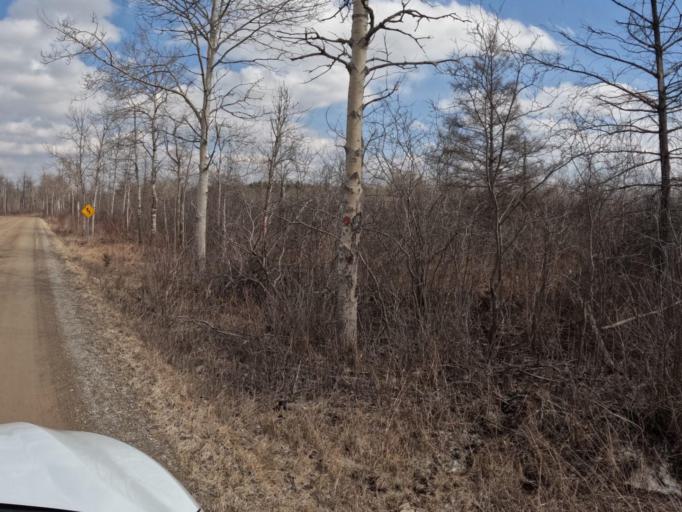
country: CA
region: Ontario
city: Shelburne
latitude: 43.9673
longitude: -80.2764
